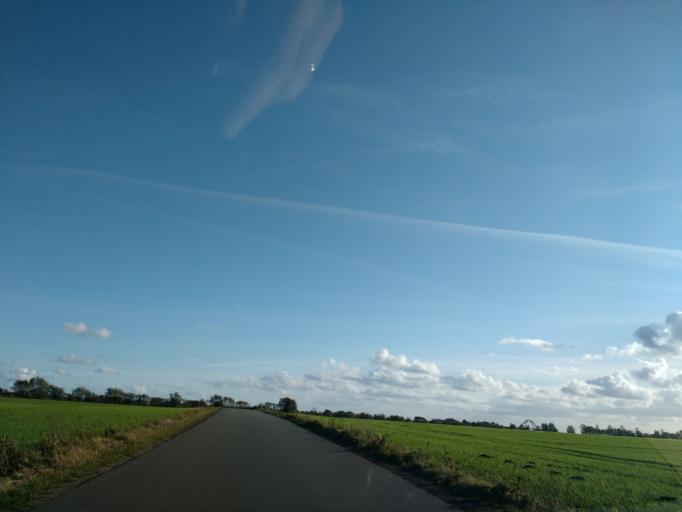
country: DE
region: Schleswig-Holstein
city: Grossenbrode
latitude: 54.4302
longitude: 11.1168
